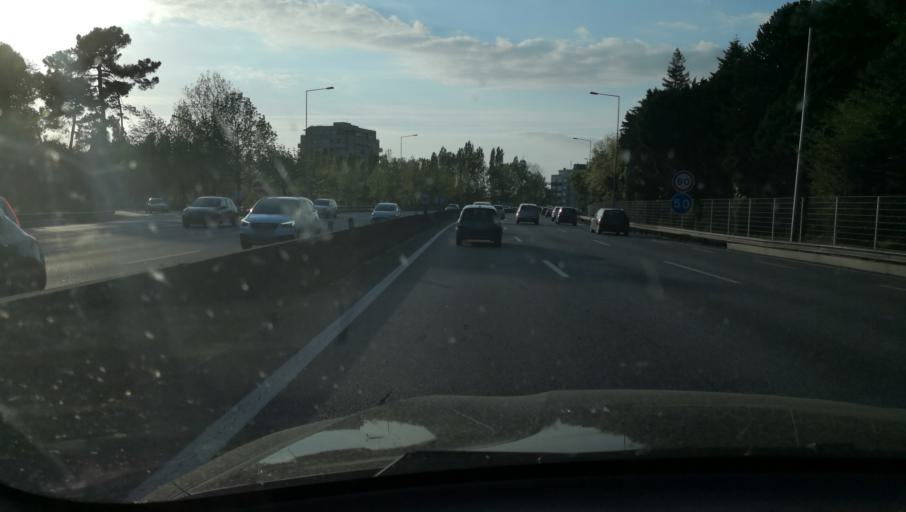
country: PT
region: Porto
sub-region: Vila Nova de Gaia
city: Canidelo
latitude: 41.1518
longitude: -8.6426
